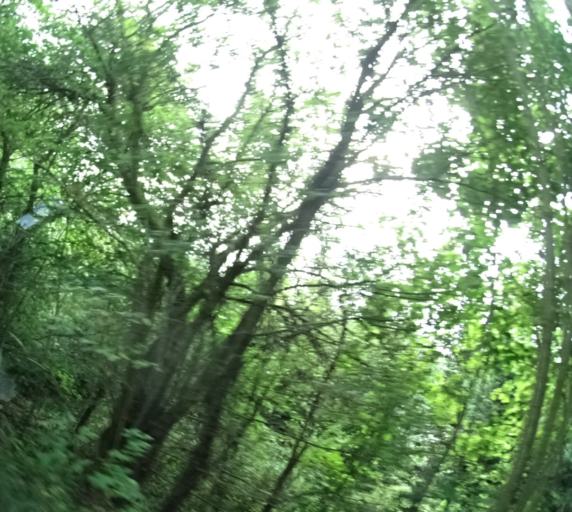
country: DK
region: Central Jutland
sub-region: Syddjurs Kommune
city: Ronde
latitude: 56.3413
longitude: 10.4857
